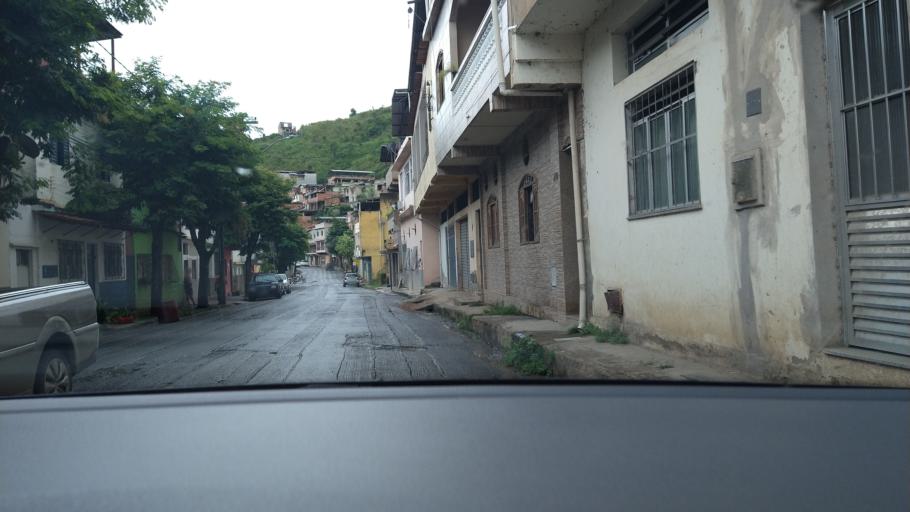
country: BR
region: Minas Gerais
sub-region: Ponte Nova
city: Ponte Nova
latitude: -20.4039
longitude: -42.8966
